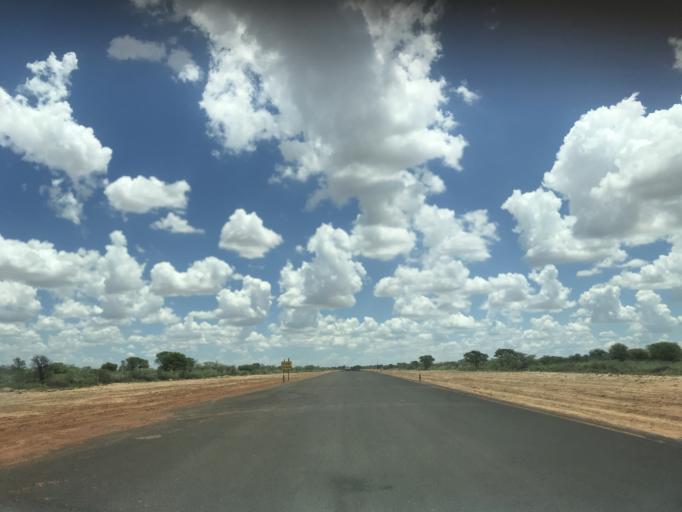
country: BW
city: Mabuli
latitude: -25.8051
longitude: 24.7029
